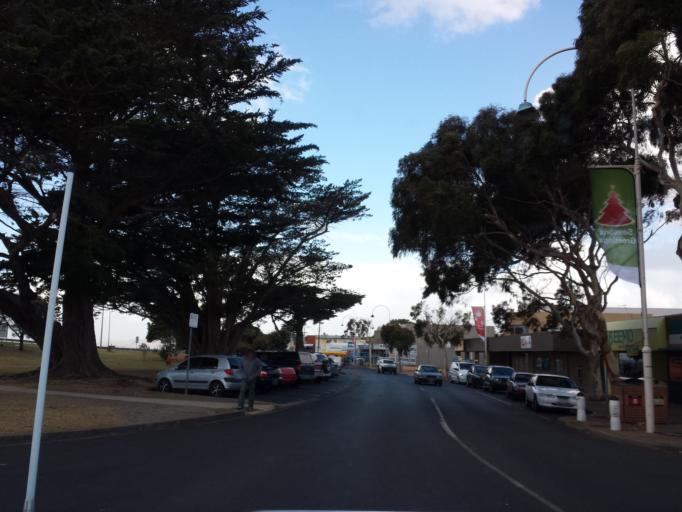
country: AU
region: Victoria
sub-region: Bass Coast
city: Phillip Island
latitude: -38.5211
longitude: 145.3673
